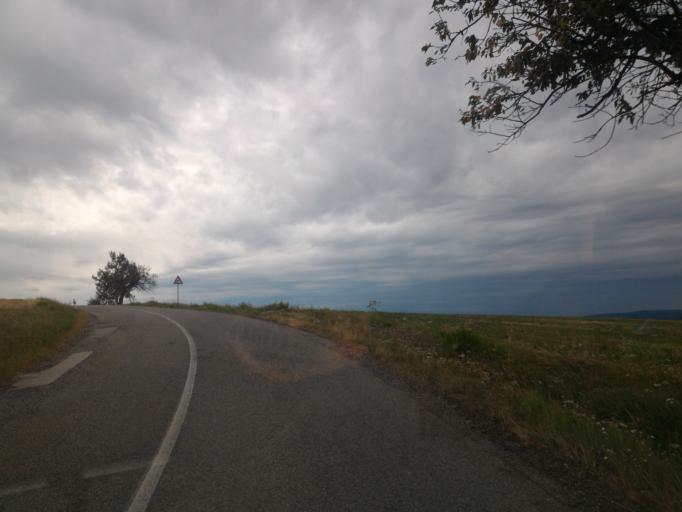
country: CZ
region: Vysocina
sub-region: Okres Jihlava
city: Trest'
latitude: 49.2386
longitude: 15.5564
